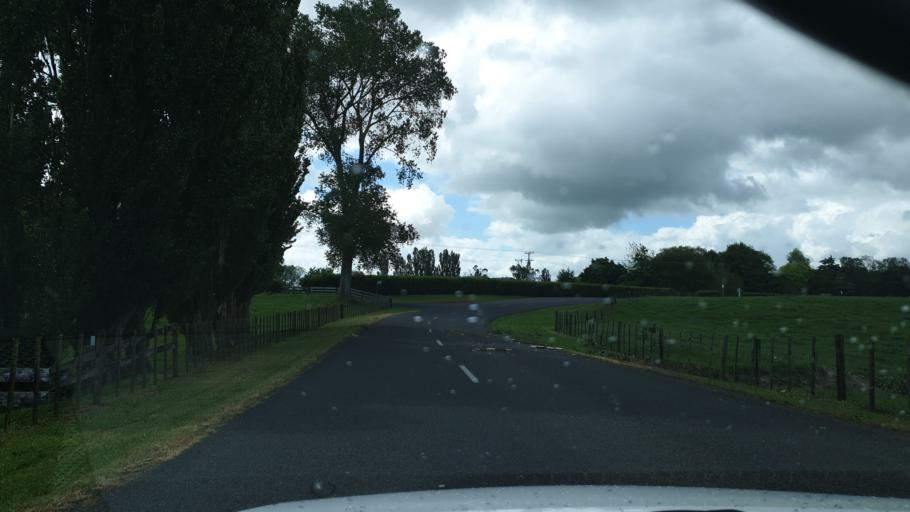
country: NZ
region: Waikato
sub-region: Matamata-Piako District
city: Matamata
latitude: -37.8708
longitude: 175.7232
